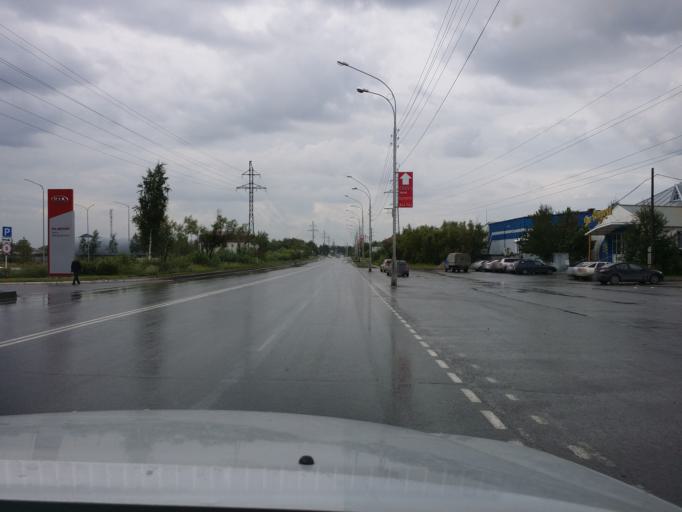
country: RU
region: Khanty-Mansiyskiy Avtonomnyy Okrug
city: Nizhnevartovsk
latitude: 60.9486
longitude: 76.5196
